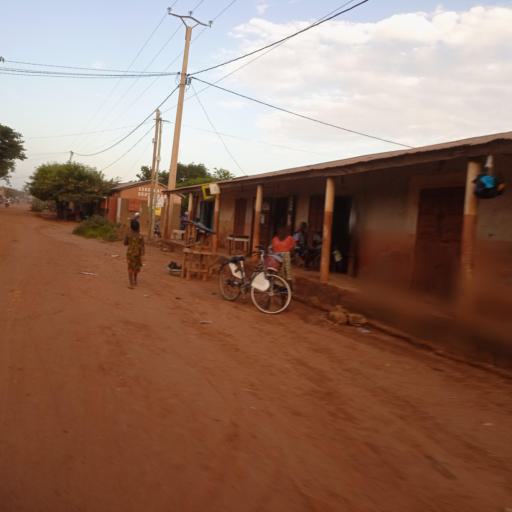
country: TG
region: Savanes
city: Dapaong
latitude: 10.8616
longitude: 0.1832
